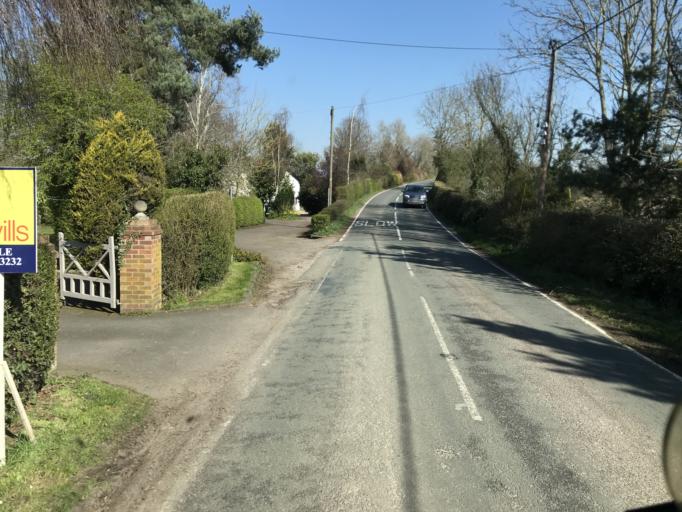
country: GB
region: England
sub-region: Cheshire West and Chester
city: Waverton
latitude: 53.1646
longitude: -2.8251
